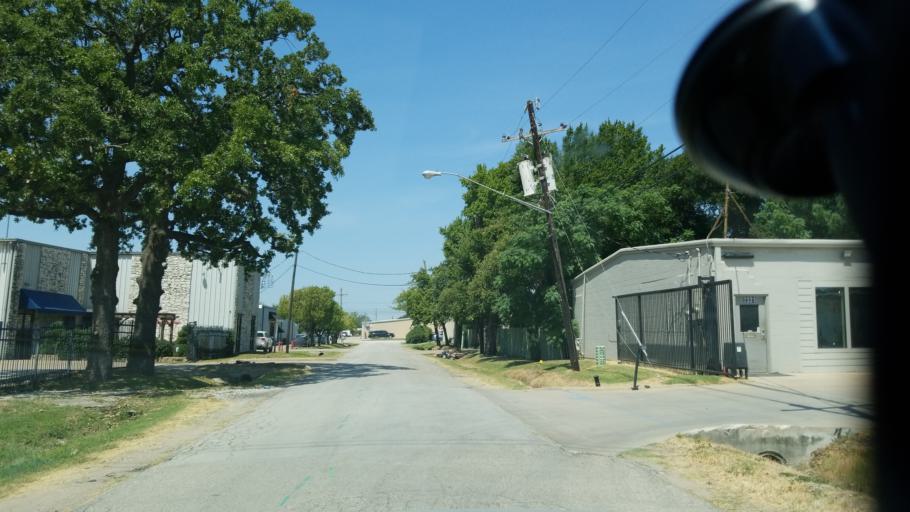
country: US
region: Texas
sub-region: Dallas County
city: Farmers Branch
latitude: 32.8914
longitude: -96.9003
